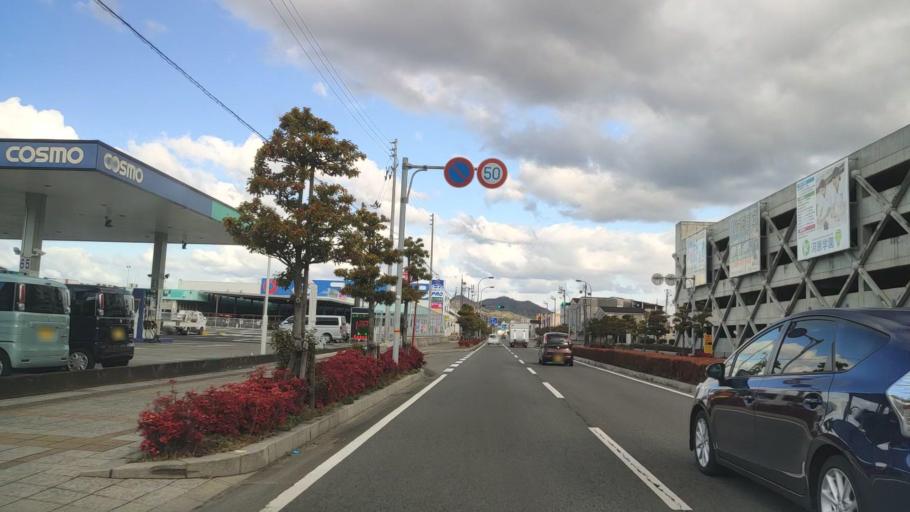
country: JP
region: Ehime
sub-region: Shikoku-chuo Shi
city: Matsuyama
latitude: 33.8504
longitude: 132.7133
